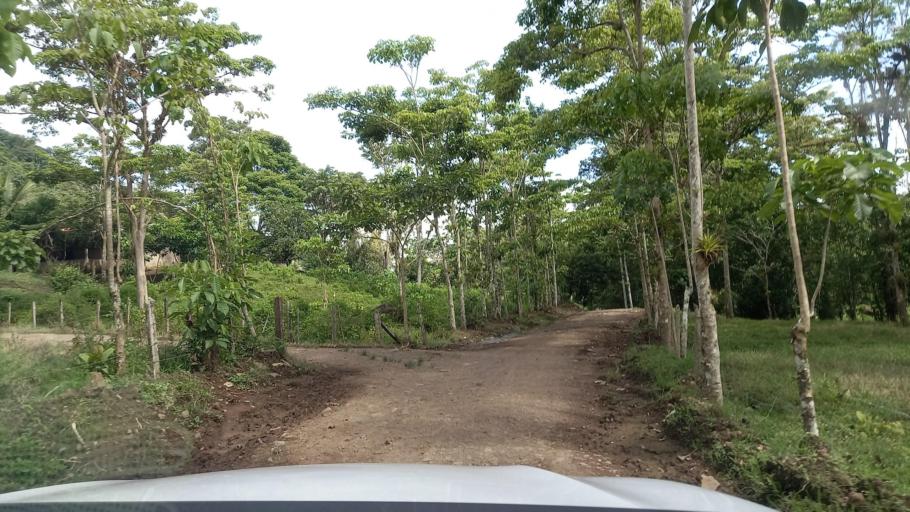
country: NI
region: Jinotega
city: San Jose de Bocay
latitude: 13.3891
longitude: -85.6926
